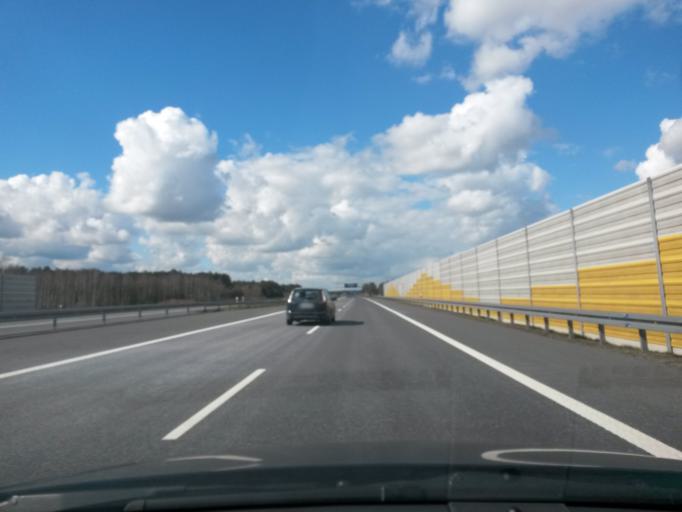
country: PL
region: Greater Poland Voivodeship
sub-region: Powiat kolski
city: Dabie
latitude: 52.0609
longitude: 18.8332
